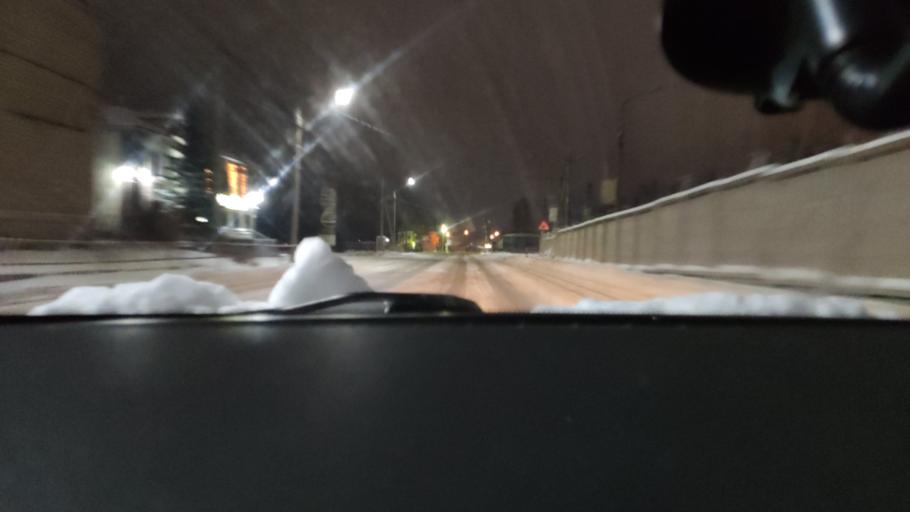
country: RU
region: Perm
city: Krasnokamsk
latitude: 58.0712
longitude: 55.7863
